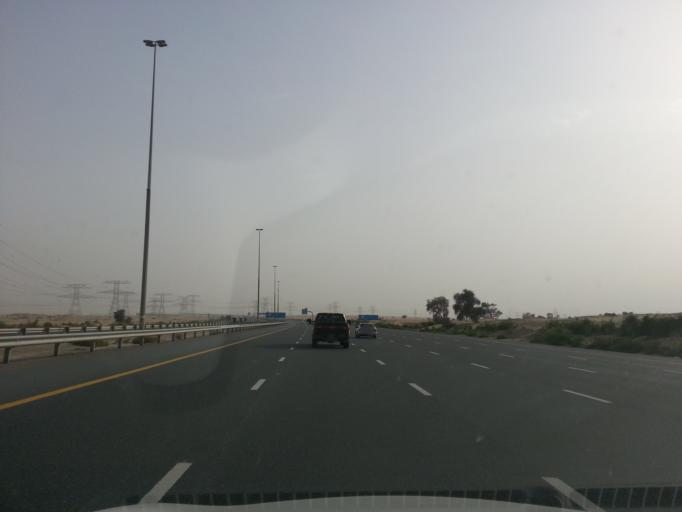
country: AE
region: Dubai
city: Dubai
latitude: 24.9941
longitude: 55.2508
